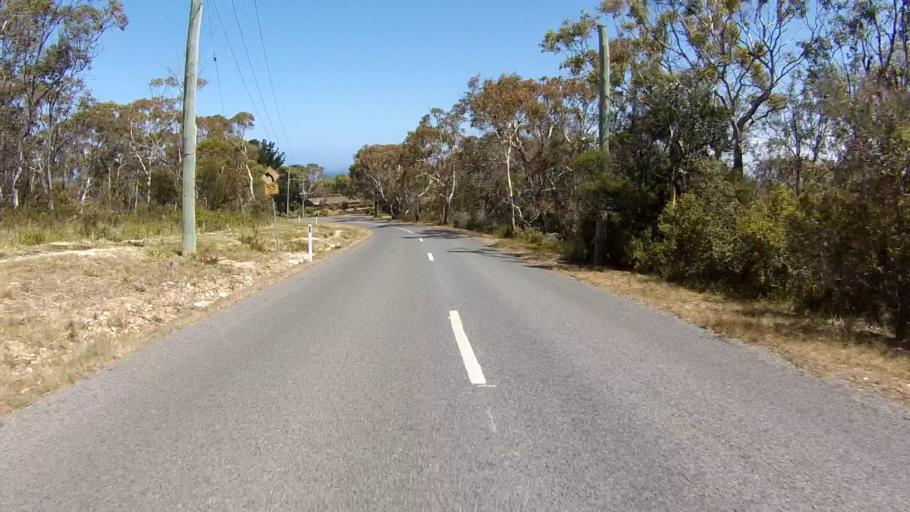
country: AU
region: Tasmania
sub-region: Clarence
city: Sandford
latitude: -43.0214
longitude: 147.4801
